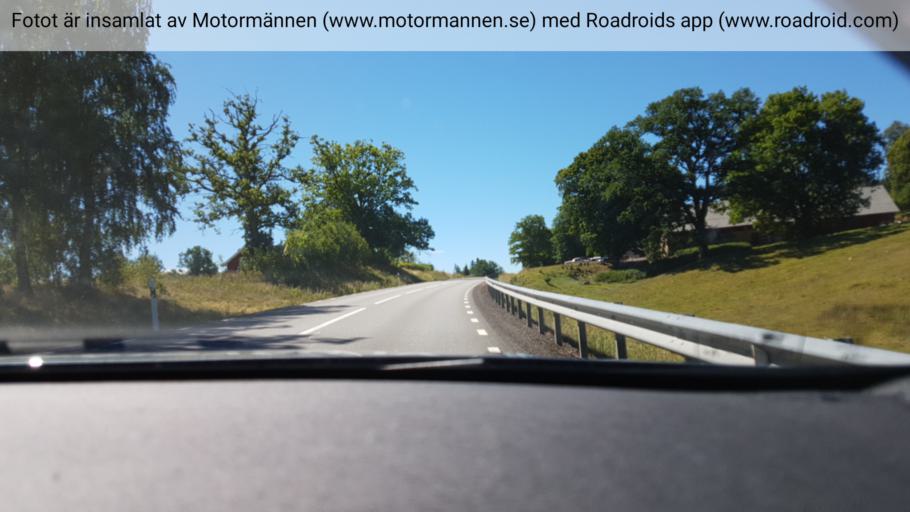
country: SE
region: Joenkoeping
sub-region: Mullsjo Kommun
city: Mullsjoe
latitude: 57.8545
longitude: 13.8572
